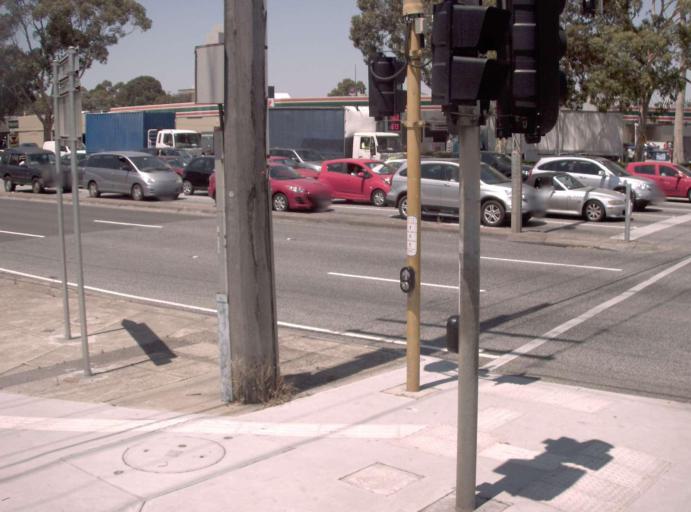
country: AU
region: Victoria
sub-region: Monash
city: Notting Hill
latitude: -37.9033
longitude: 145.1616
